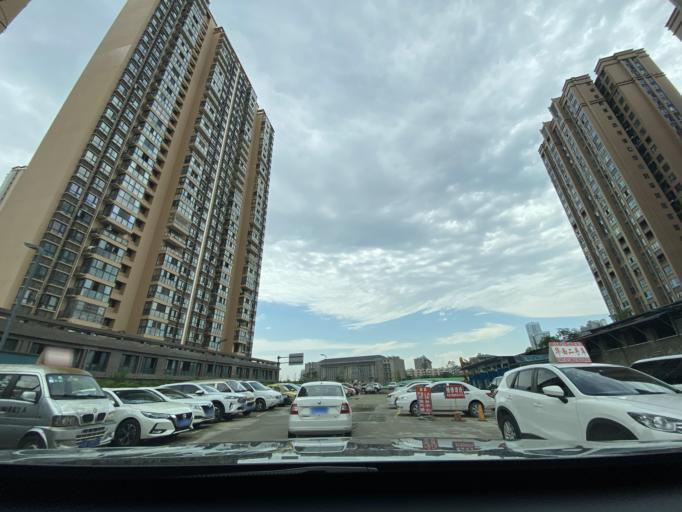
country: CN
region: Sichuan
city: Dongsheng
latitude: 30.5126
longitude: 104.0391
